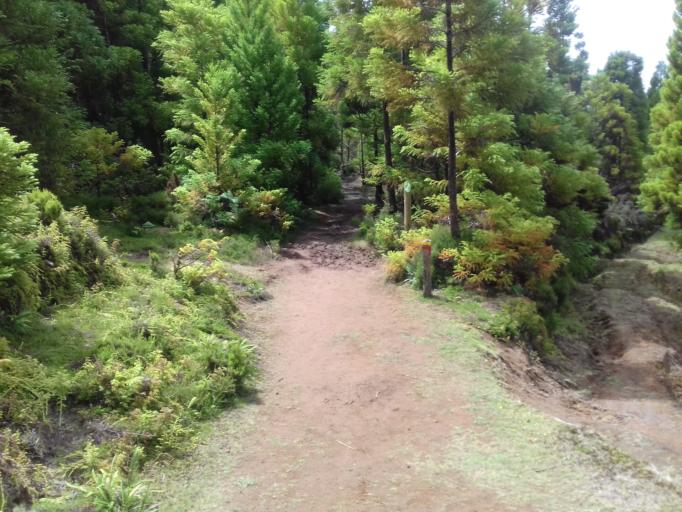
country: PT
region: Azores
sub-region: Praia da Vitoria
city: Biscoitos
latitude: 38.7313
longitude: -27.2824
